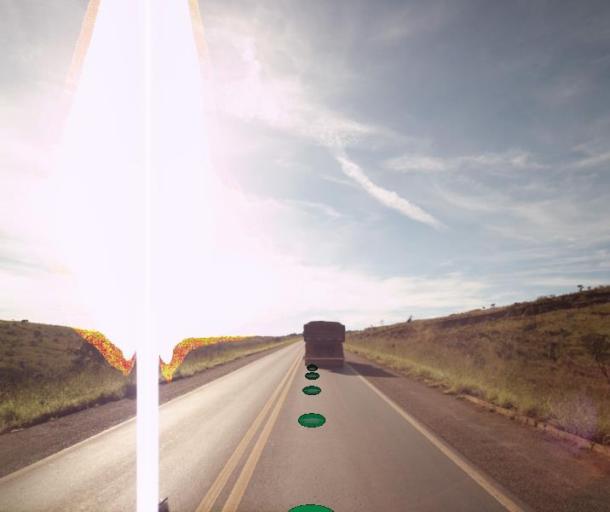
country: BR
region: Federal District
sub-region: Brasilia
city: Brasilia
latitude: -15.7547
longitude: -48.3425
